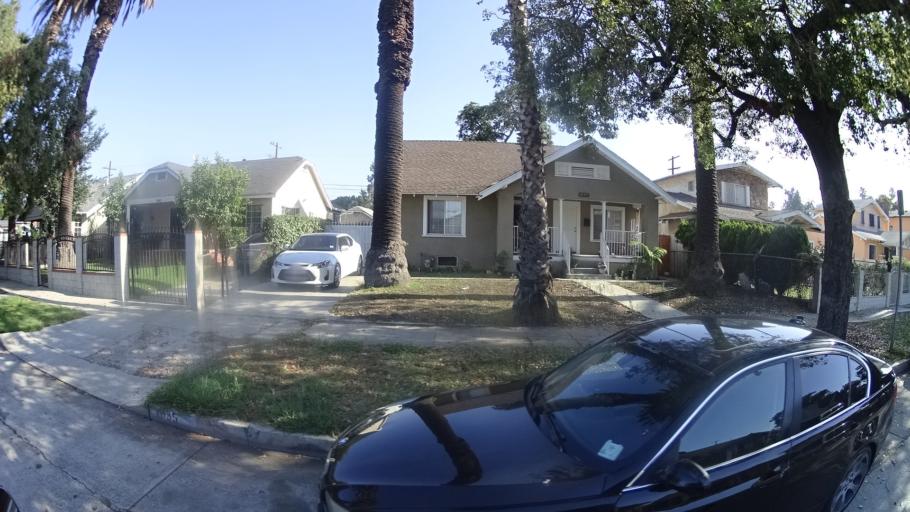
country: US
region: California
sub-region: Los Angeles County
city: Westmont
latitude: 33.9754
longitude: -118.2931
